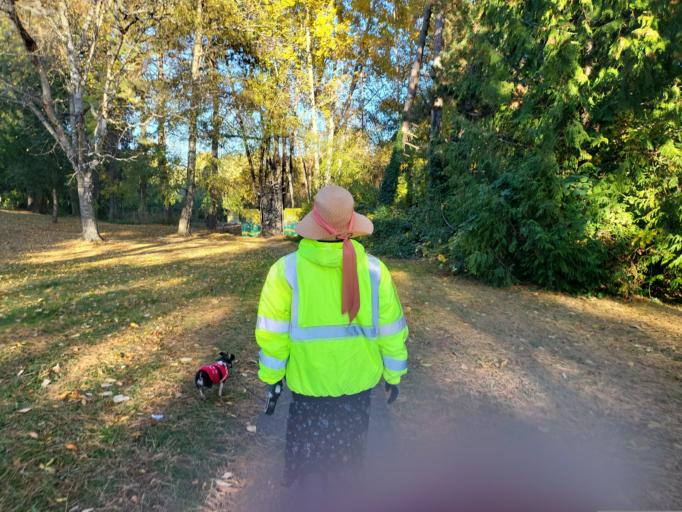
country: US
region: Washington
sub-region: King County
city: Bryn Mawr-Skyway
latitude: 47.5245
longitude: -122.2634
